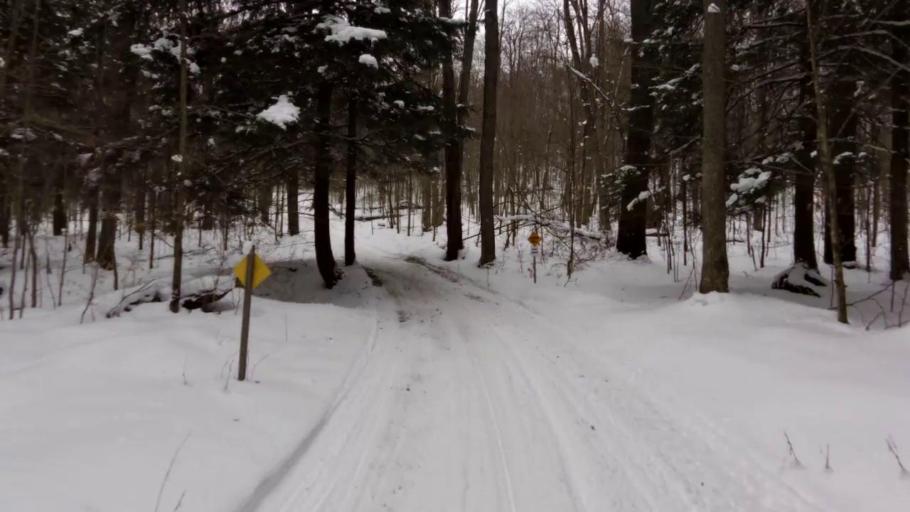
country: US
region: Pennsylvania
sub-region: McKean County
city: Bradford
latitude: 42.0277
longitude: -78.7279
